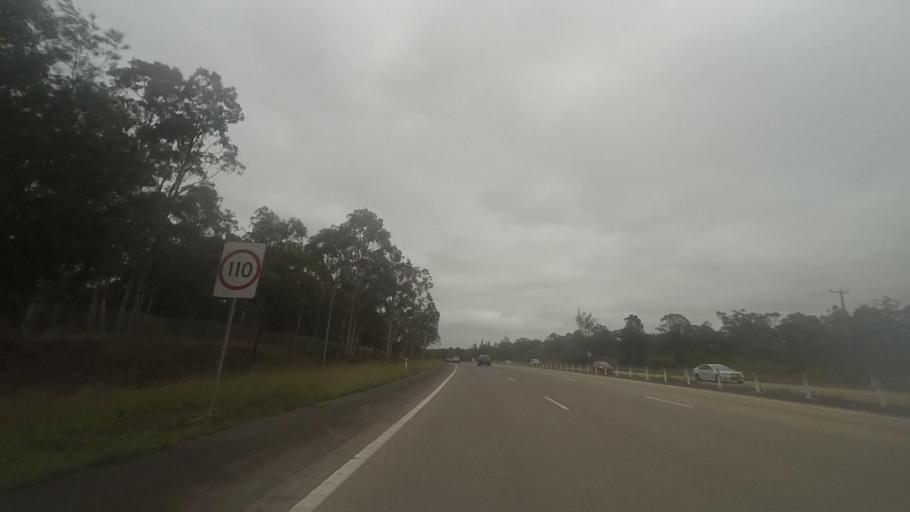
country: AU
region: New South Wales
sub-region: Port Stephens Shire
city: Medowie
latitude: -32.6835
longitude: 151.8130
